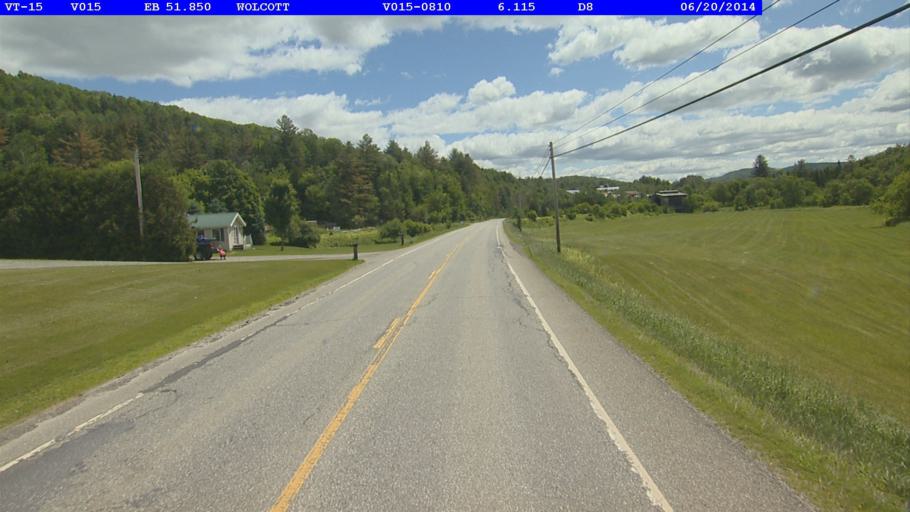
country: US
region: Vermont
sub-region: Caledonia County
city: Hardwick
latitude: 44.5341
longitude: -72.4310
